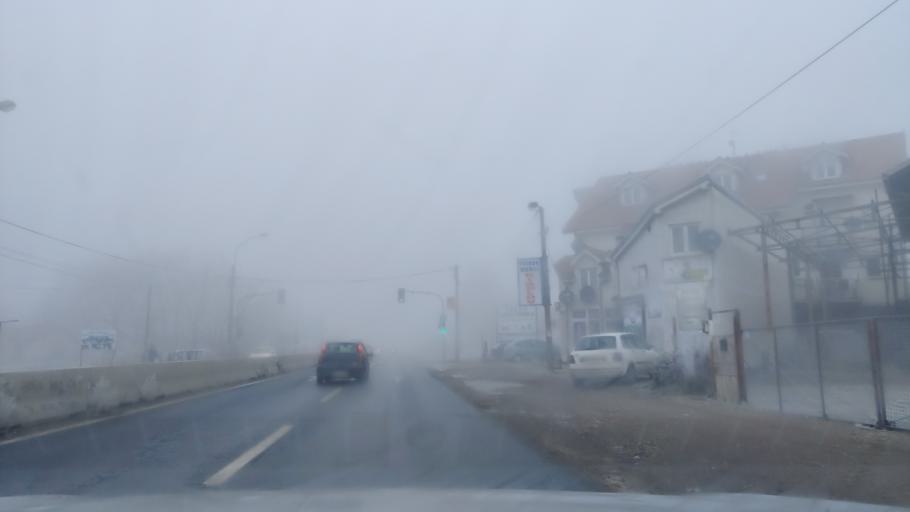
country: RS
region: Central Serbia
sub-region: Belgrade
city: Stari Grad
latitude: 44.8726
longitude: 20.4709
